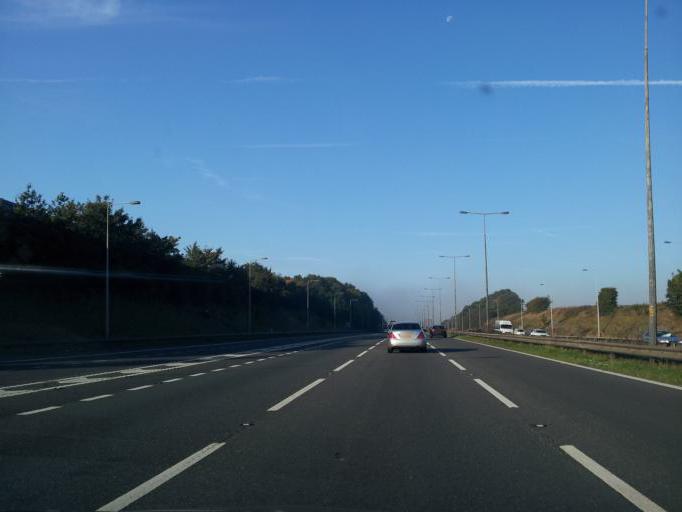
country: GB
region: England
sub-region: City and Borough of Leeds
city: Drighlington
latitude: 53.7460
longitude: -1.6511
